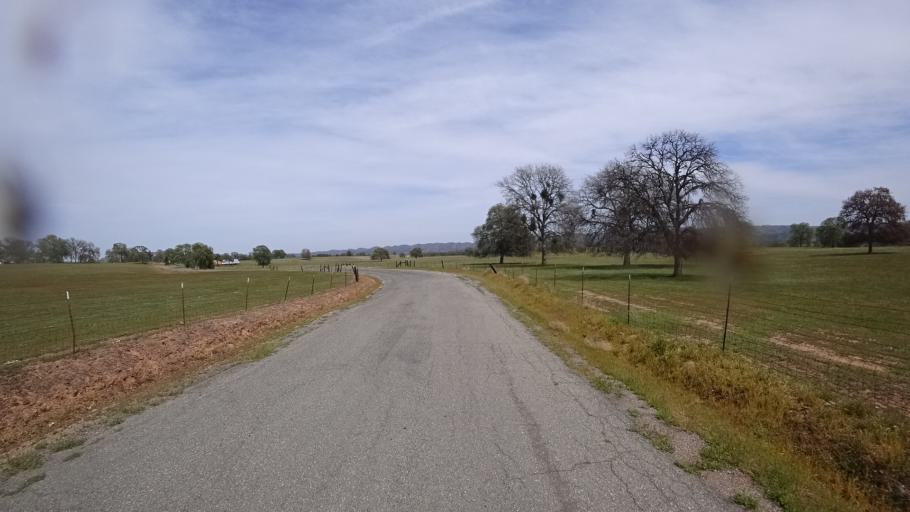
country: US
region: California
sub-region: Glenn County
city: Willows
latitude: 39.5860
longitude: -122.5782
